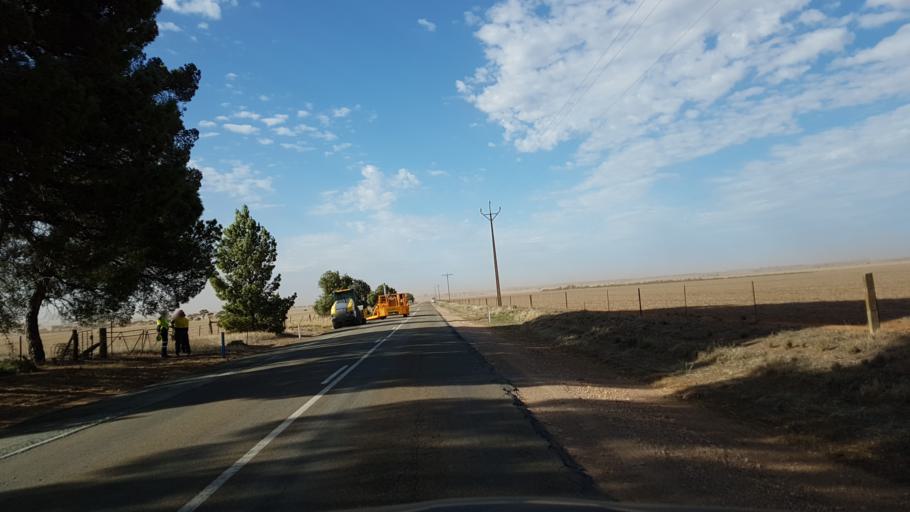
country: AU
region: South Australia
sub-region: Clare and Gilbert Valleys
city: Clare
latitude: -33.8819
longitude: 138.4794
